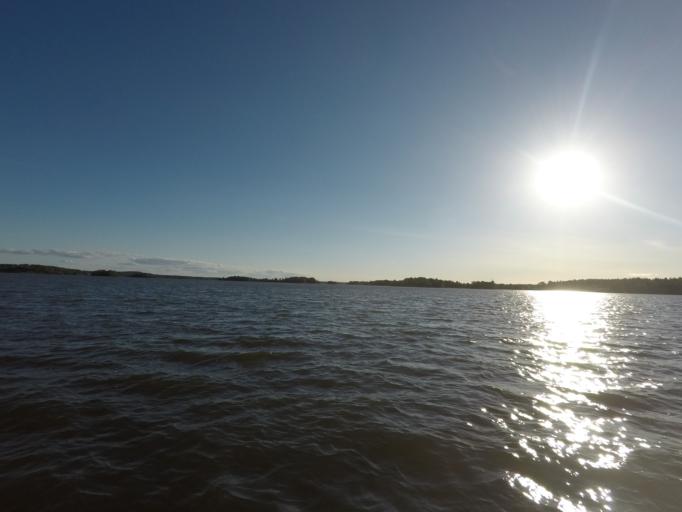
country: SE
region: Soedermanland
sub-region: Eskilstuna Kommun
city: Torshalla
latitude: 59.4811
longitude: 16.4729
